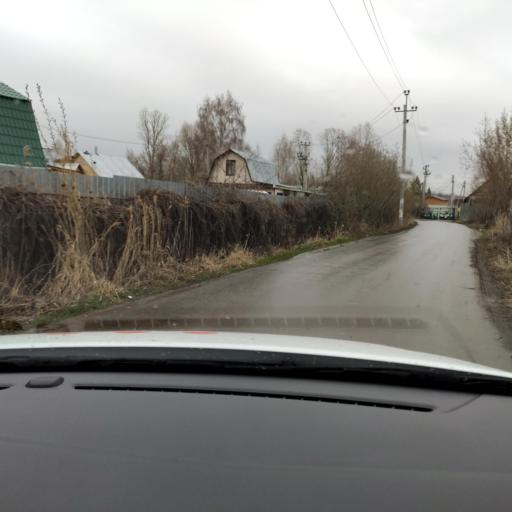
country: RU
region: Tatarstan
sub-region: Gorod Kazan'
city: Kazan
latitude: 55.6897
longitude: 49.0713
